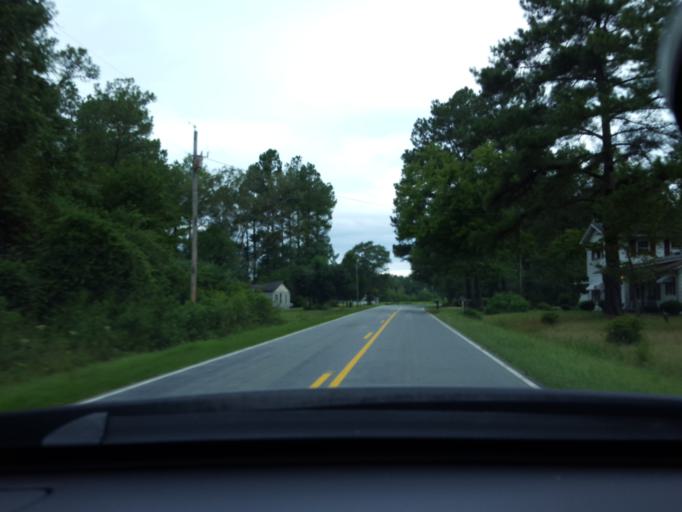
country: US
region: North Carolina
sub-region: Sampson County
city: Clinton
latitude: 34.7798
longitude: -78.3597
